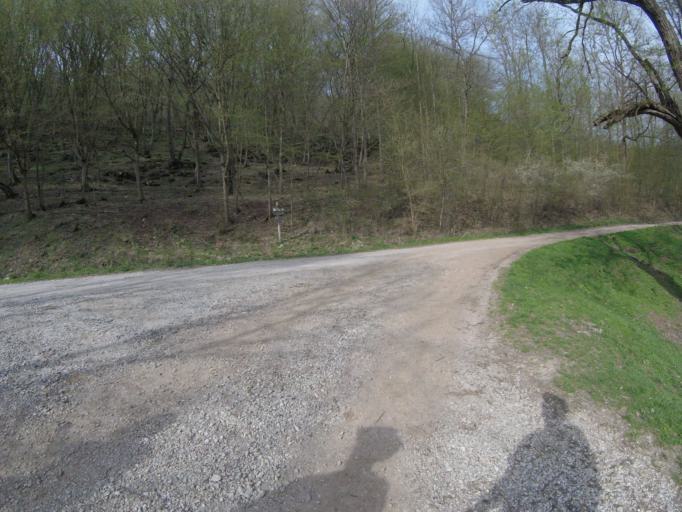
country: HU
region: Borsod-Abauj-Zemplen
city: Szendro
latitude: 48.5395
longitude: 20.6632
